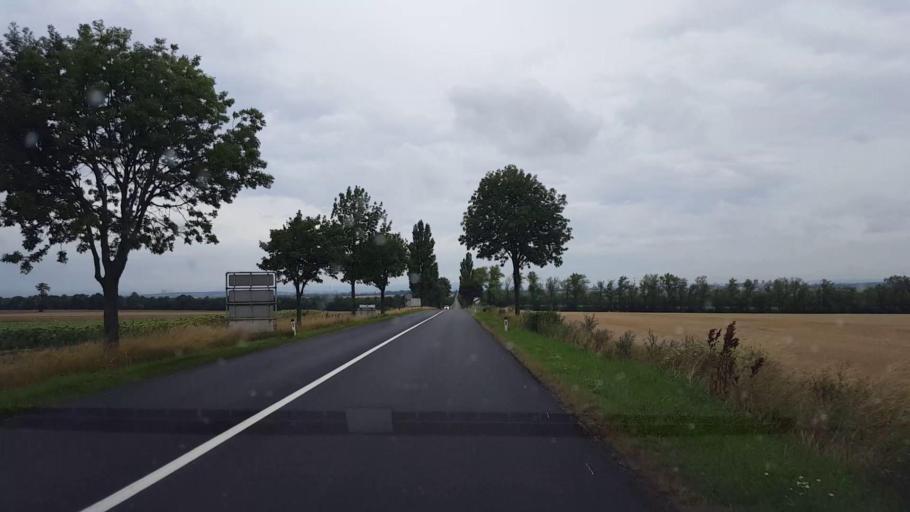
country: AT
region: Lower Austria
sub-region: Politischer Bezirk Wien-Umgebung
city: Rauchenwarth
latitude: 48.1068
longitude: 16.5295
